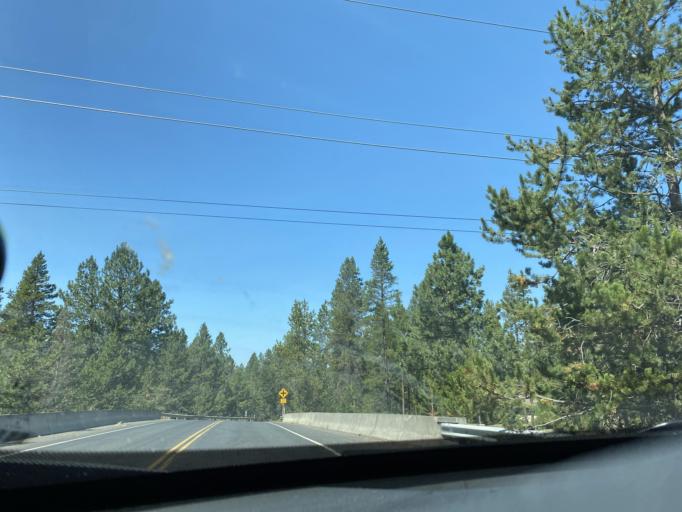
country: US
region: Oregon
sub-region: Deschutes County
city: Sunriver
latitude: 43.8936
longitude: -121.4151
